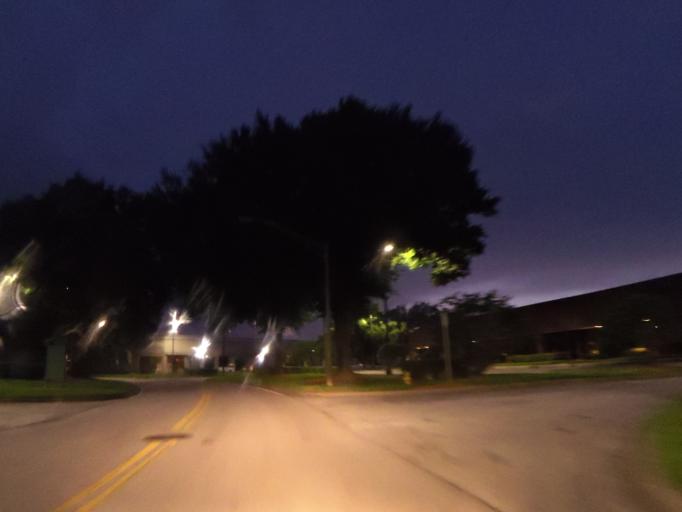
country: US
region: Florida
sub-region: Saint Johns County
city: Fruit Cove
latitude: 30.2040
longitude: -81.5578
